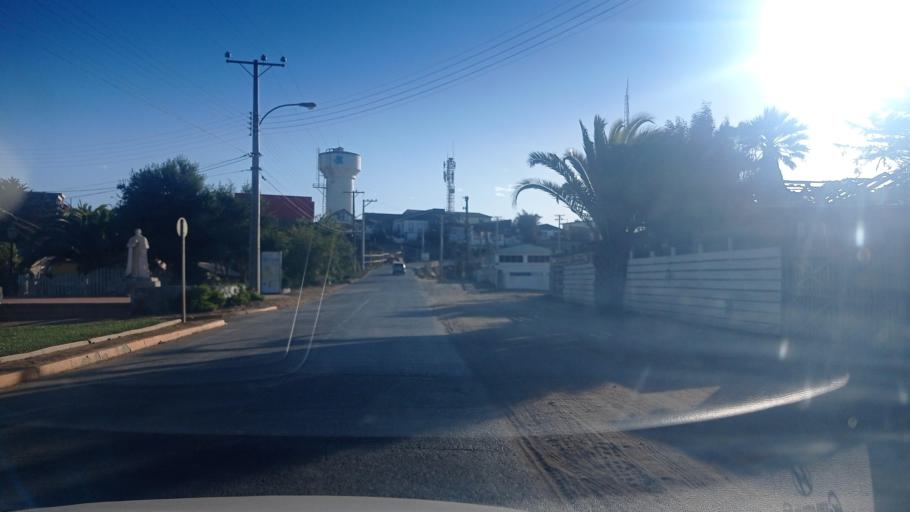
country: CL
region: O'Higgins
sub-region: Provincia de Colchagua
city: Santa Cruz
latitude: -34.3858
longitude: -72.0004
